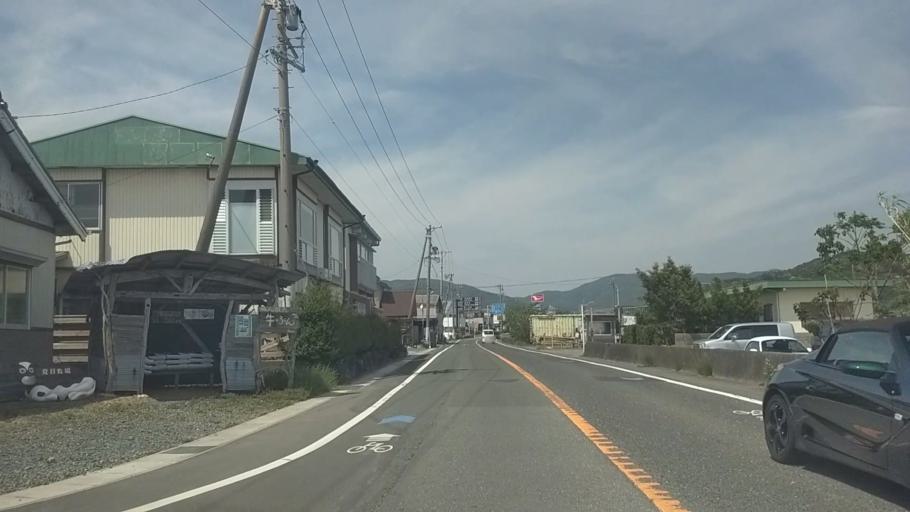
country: JP
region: Shizuoka
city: Kosai-shi
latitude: 34.7988
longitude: 137.5486
